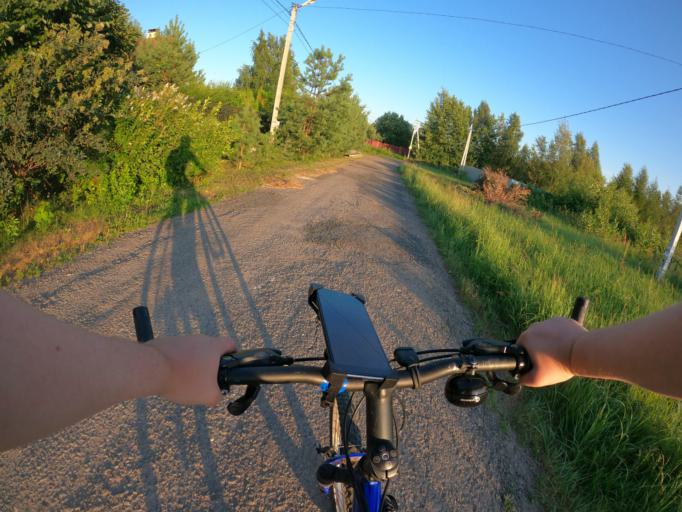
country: RU
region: Moskovskaya
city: Beloozerskiy
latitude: 55.4609
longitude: 38.4255
